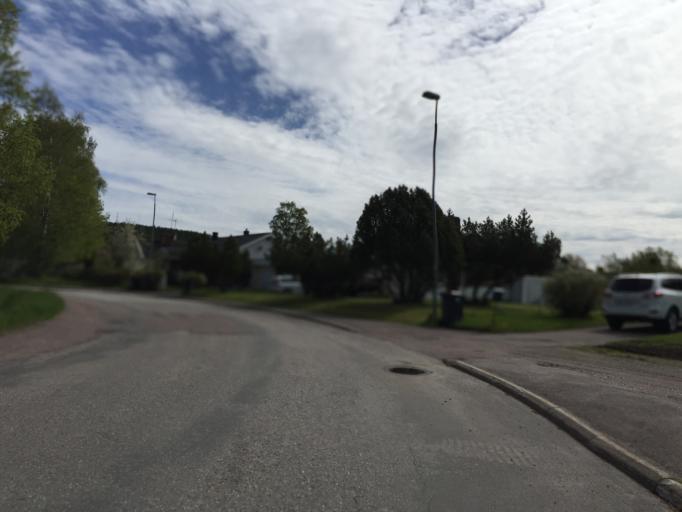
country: SE
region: Dalarna
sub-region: Ludvika Kommun
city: Ludvika
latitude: 60.1349
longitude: 15.1686
